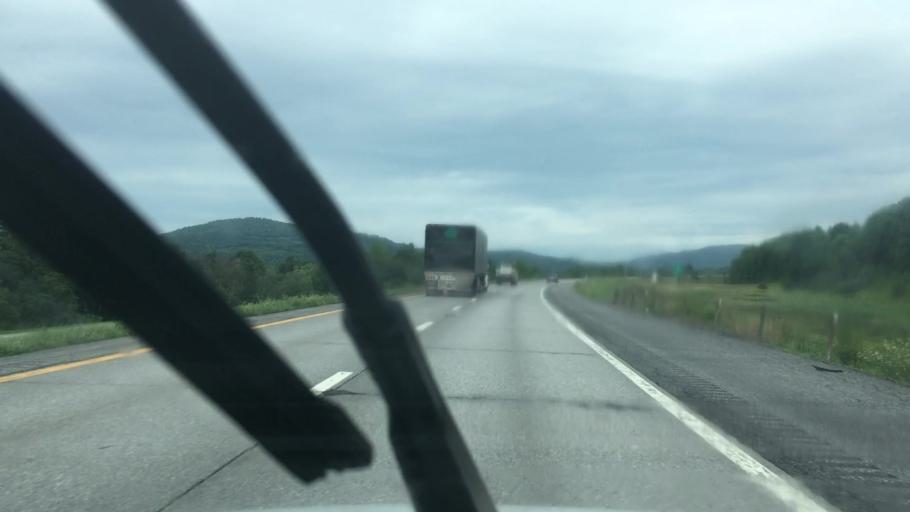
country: US
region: New York
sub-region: Otsego County
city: Worcester
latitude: 42.5842
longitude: -74.7581
